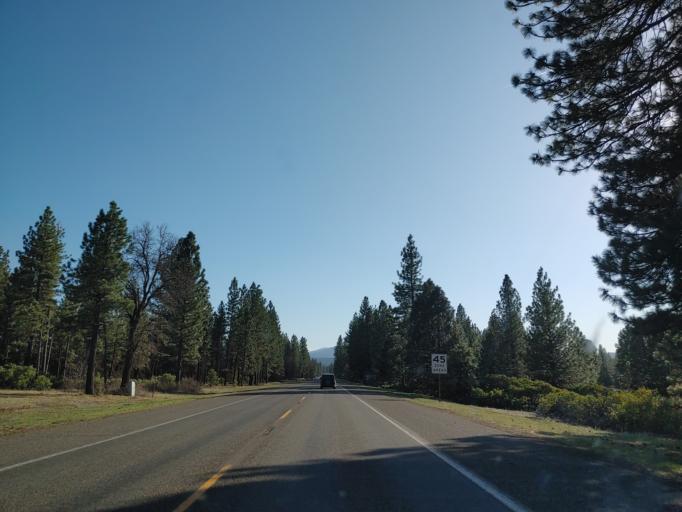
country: US
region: California
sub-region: Shasta County
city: Burney
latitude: 40.8980
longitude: -121.6455
